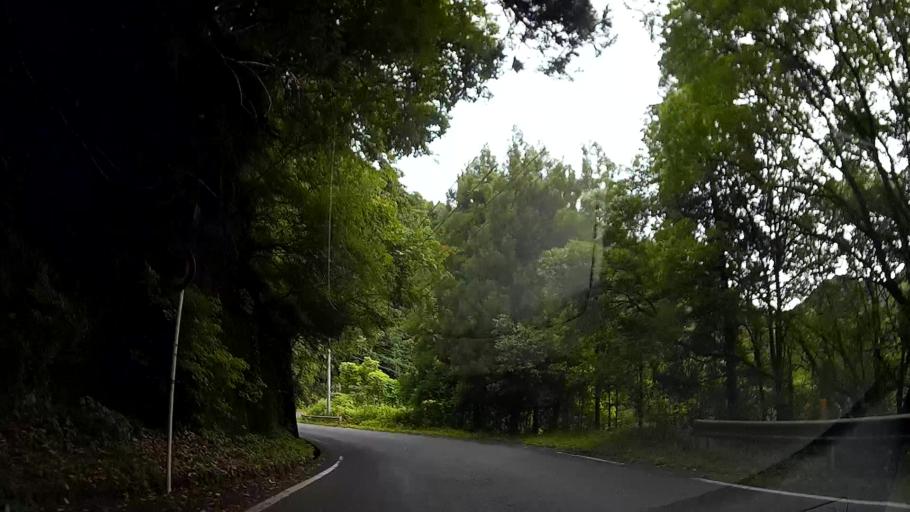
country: JP
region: Kumamoto
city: Kikuchi
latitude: 33.0962
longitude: 130.9572
